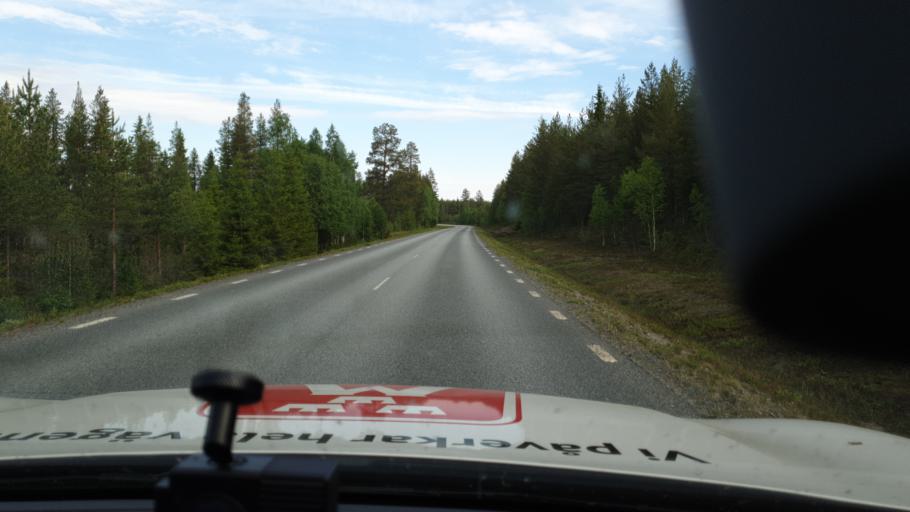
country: SE
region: Vaesterbotten
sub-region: Lycksele Kommun
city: Soderfors
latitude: 65.1434
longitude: 18.2640
